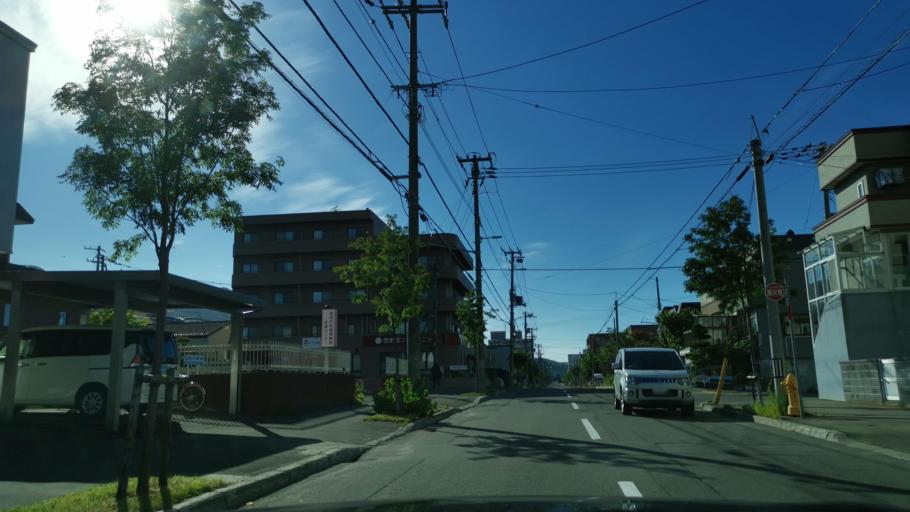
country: JP
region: Hokkaido
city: Sapporo
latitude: 43.0820
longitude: 141.2785
